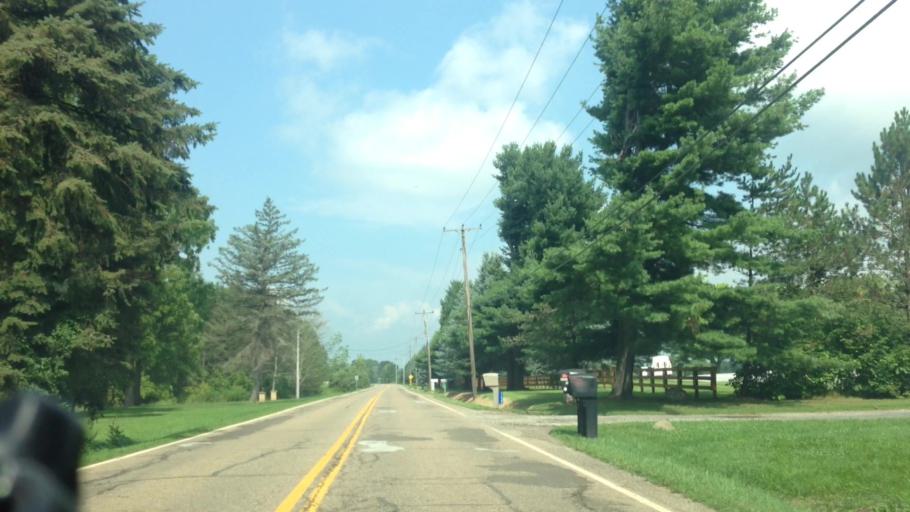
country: US
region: Ohio
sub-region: Stark County
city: Canal Fulton
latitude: 40.8394
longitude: -81.5746
